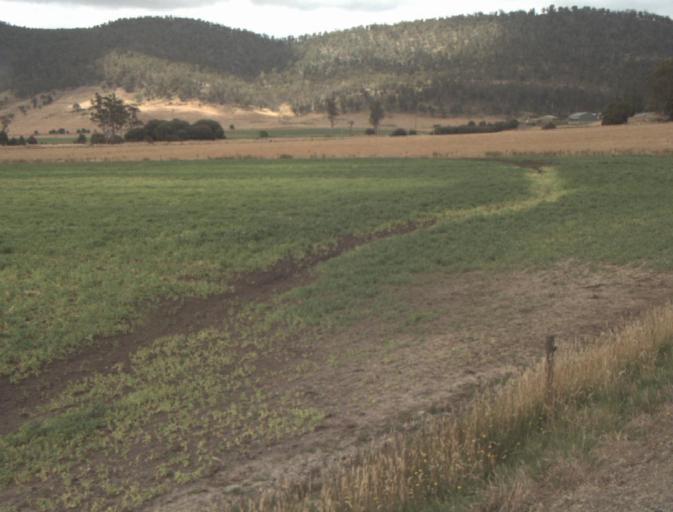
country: AU
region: Tasmania
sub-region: Northern Midlands
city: Evandale
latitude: -41.4798
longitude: 147.4435
